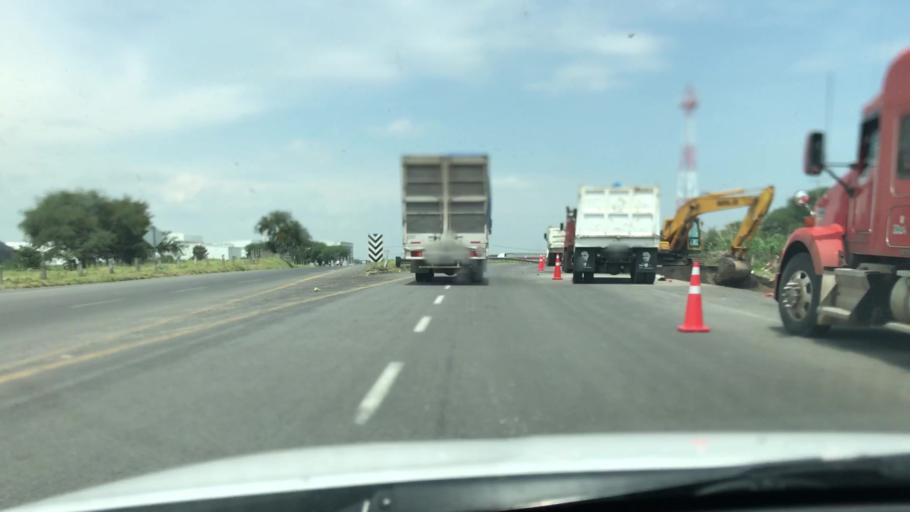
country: MX
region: Michoacan
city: Vistahermosa de Negrete
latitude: 20.2689
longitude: -102.4443
